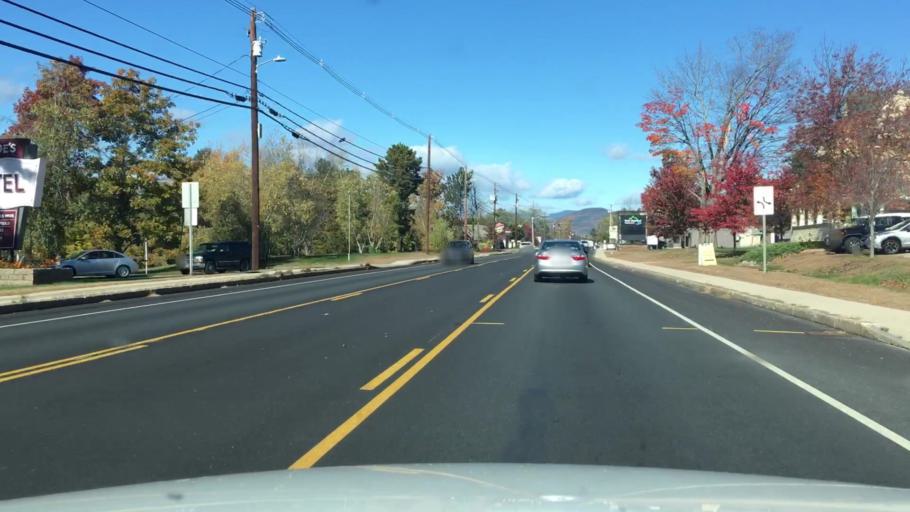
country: US
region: New Hampshire
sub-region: Carroll County
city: North Conway
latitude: 44.0298
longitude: -71.1198
